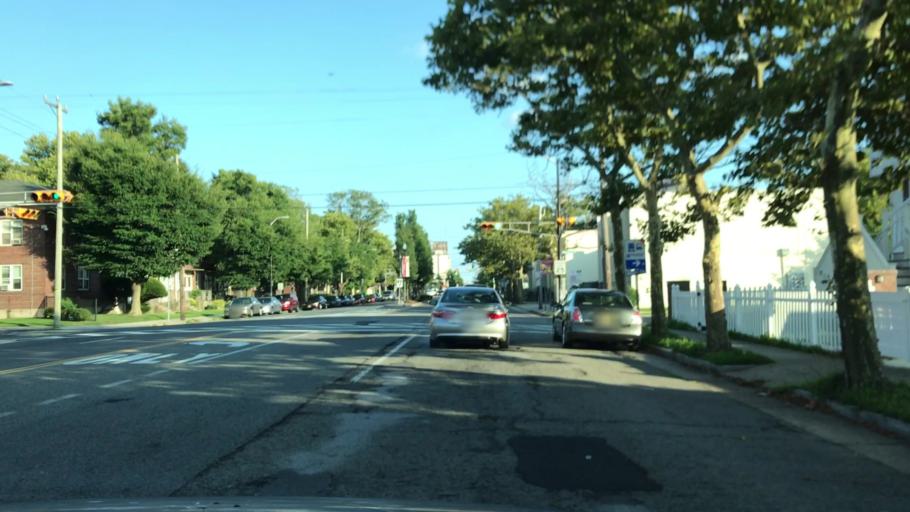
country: US
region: New Jersey
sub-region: Atlantic County
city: Atlantic City
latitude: 39.3650
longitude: -74.4349
